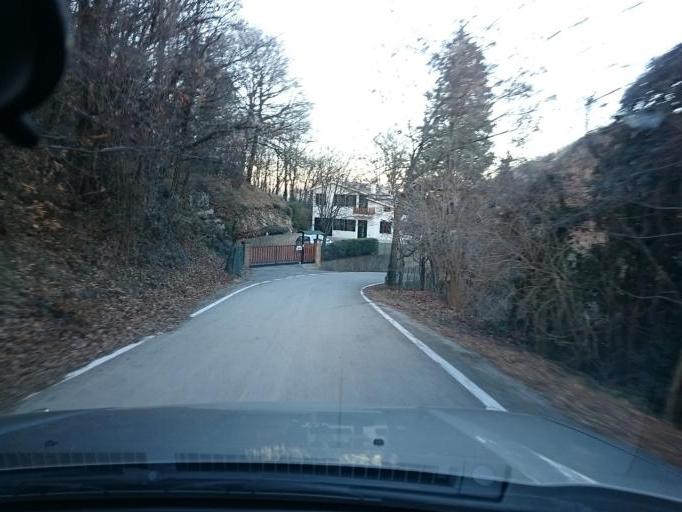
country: IT
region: Veneto
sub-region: Provincia di Padova
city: Bastia
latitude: 45.3575
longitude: 11.6607
